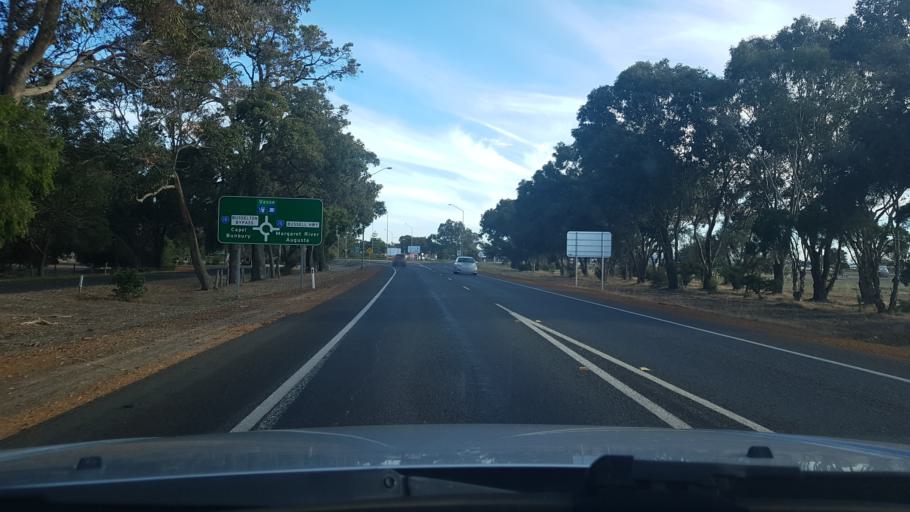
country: AU
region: Western Australia
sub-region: Busselton
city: Vasse
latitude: -33.6727
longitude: 115.2546
